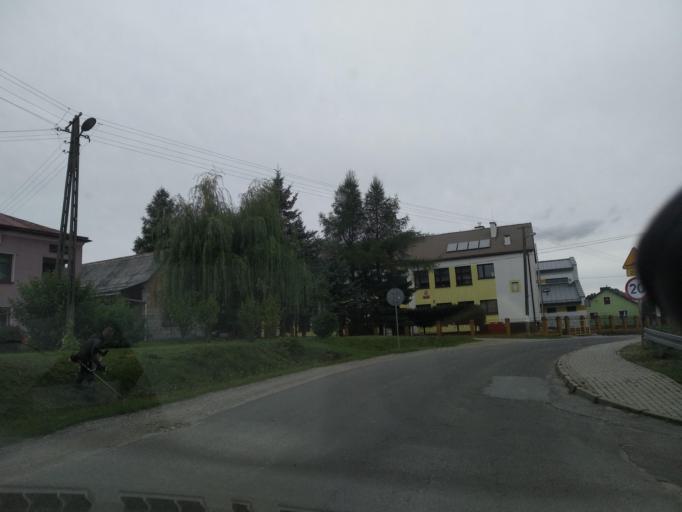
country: PL
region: Subcarpathian Voivodeship
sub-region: Powiat krosnienski
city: Iwonicz-Zdroj
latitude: 49.5802
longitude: 21.7514
